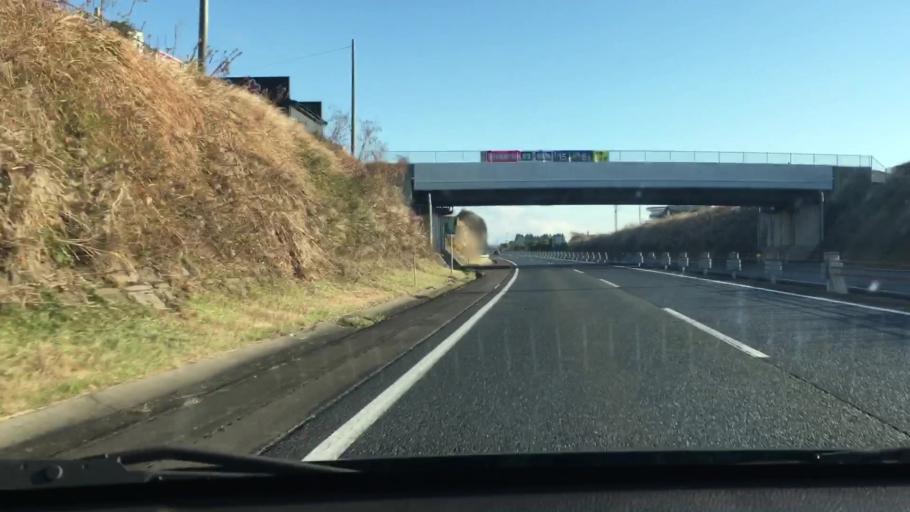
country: JP
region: Kagoshima
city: Kajiki
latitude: 31.8050
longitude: 130.7095
